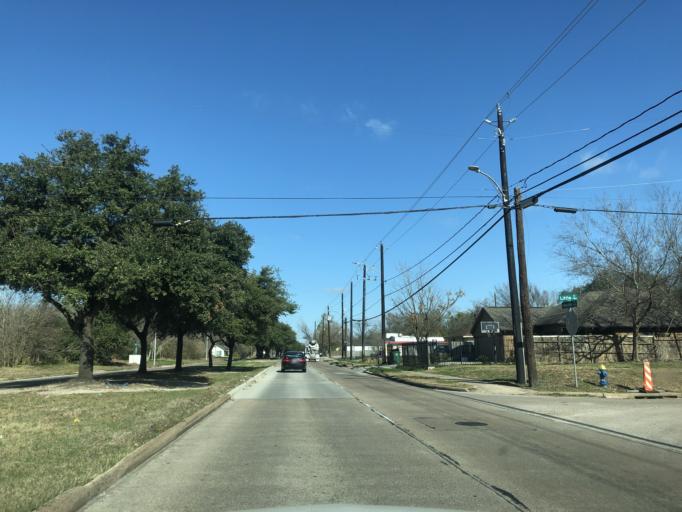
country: US
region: Texas
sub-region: Harris County
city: Jacinto City
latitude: 29.8176
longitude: -95.2845
